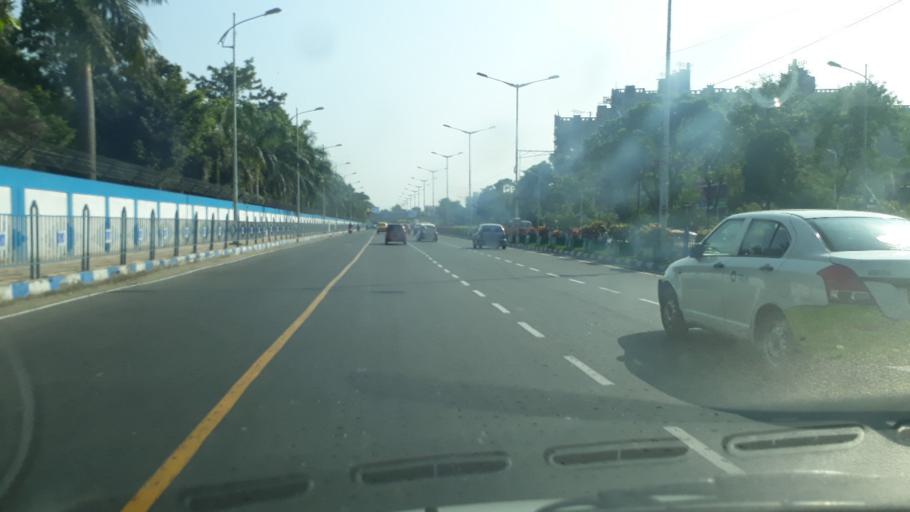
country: IN
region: West Bengal
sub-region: Kolkata
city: Kolkata
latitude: 22.5661
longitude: 88.4065
